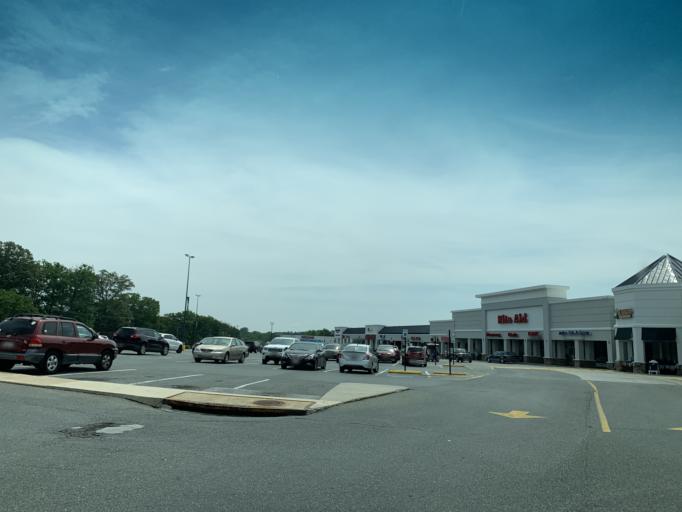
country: US
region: Maryland
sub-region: Baltimore County
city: Perry Hall
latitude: 39.3971
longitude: -76.4778
